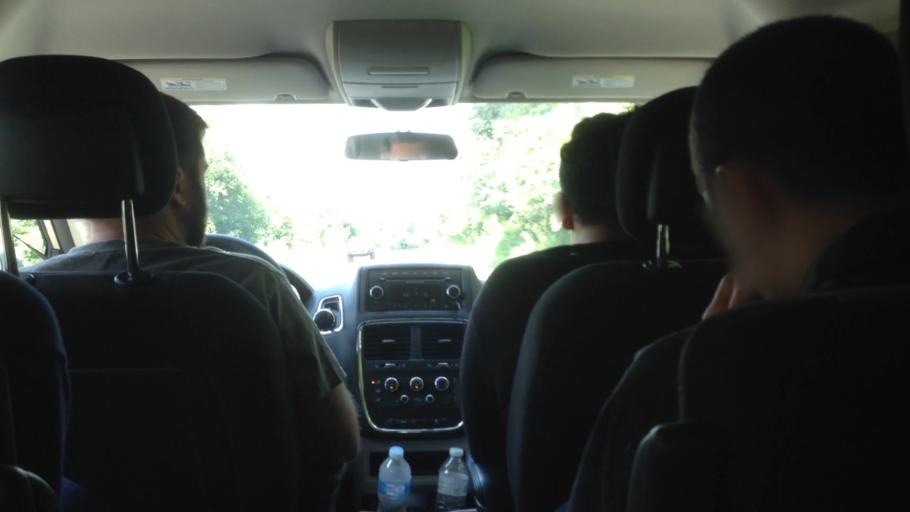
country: US
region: New York
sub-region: Dutchess County
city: Tivoli
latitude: 42.1001
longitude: -73.8961
